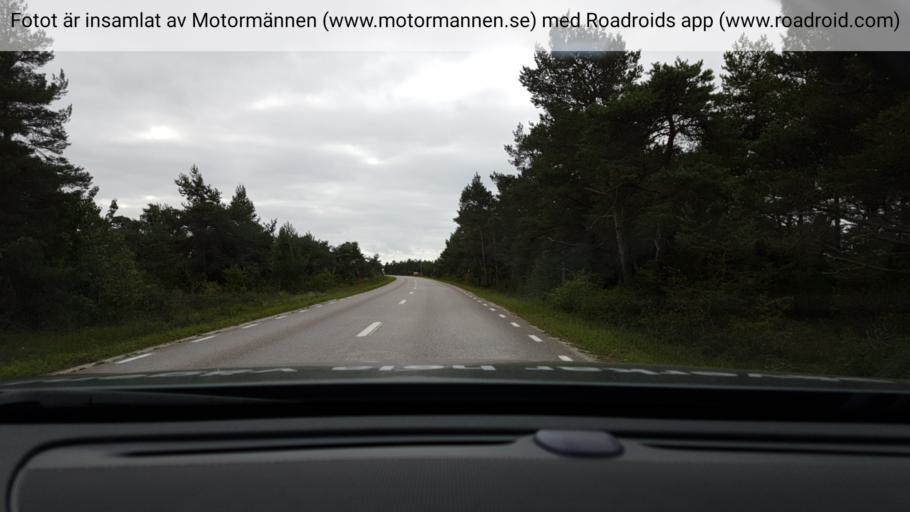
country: SE
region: Gotland
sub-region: Gotland
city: Hemse
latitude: 57.1226
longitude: 18.2761
